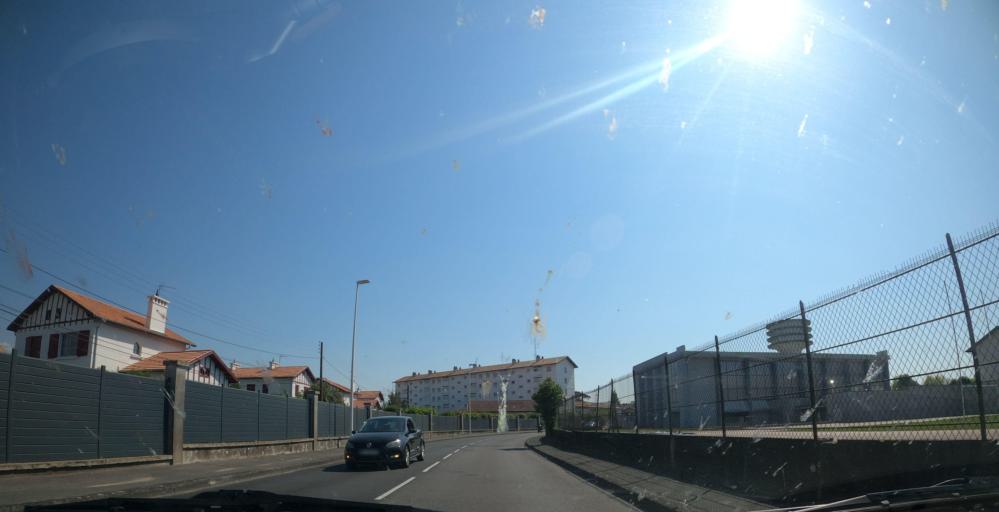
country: FR
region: Aquitaine
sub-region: Departement des Pyrenees-Atlantiques
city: Bayonne
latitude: 43.4778
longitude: -1.4817
